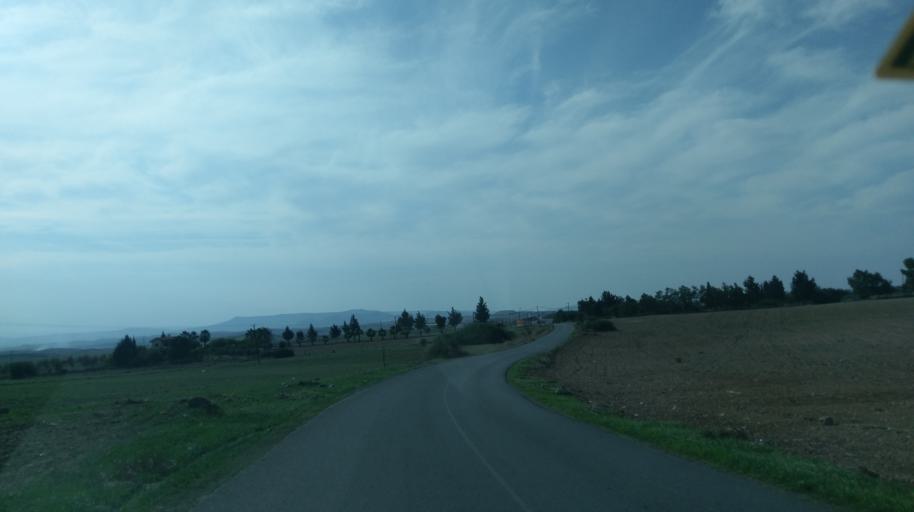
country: CY
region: Keryneia
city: Lapithos
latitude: 35.2819
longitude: 33.2281
